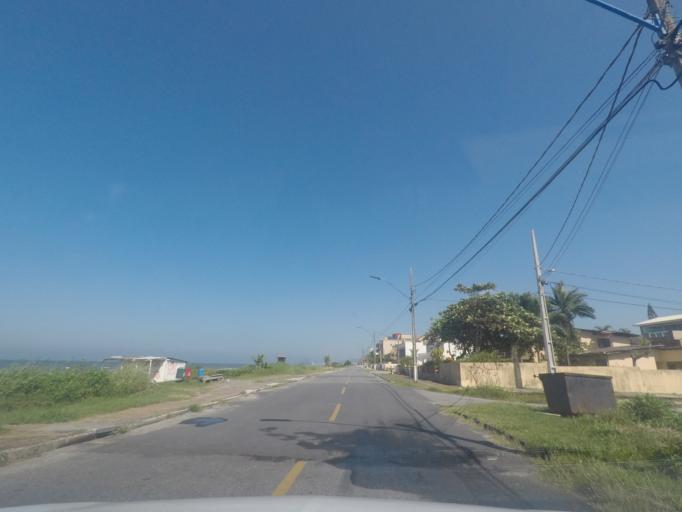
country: BR
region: Parana
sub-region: Pontal Do Parana
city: Pontal do Parana
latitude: -25.7597
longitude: -48.5059
